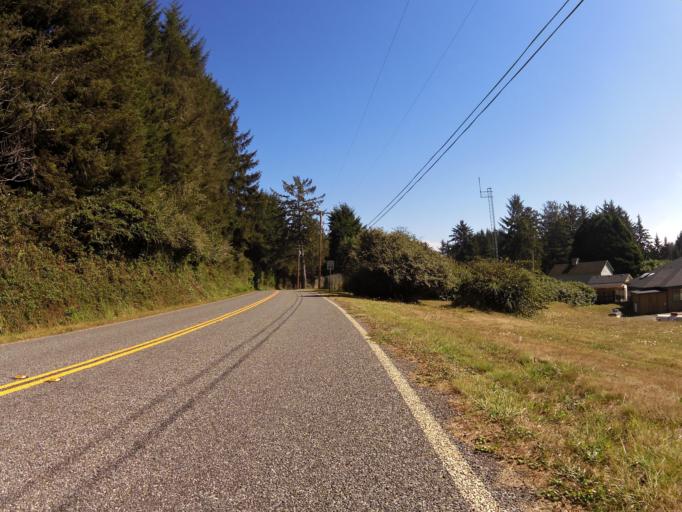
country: US
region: Oregon
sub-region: Curry County
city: Harbor
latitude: 41.9523
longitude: -124.2011
